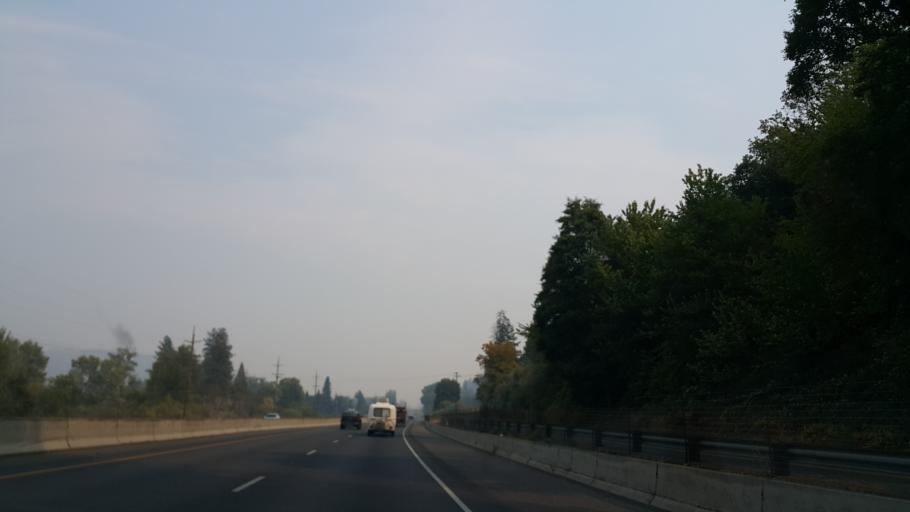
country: US
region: Oregon
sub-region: Jackson County
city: Gold Hill
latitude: 42.4287
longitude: -123.0531
